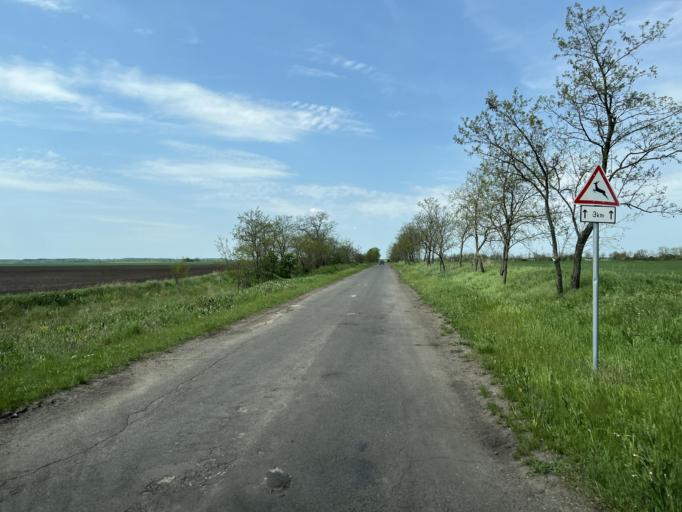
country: HU
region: Pest
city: Tapiogyorgye
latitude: 47.2973
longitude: 19.9874
